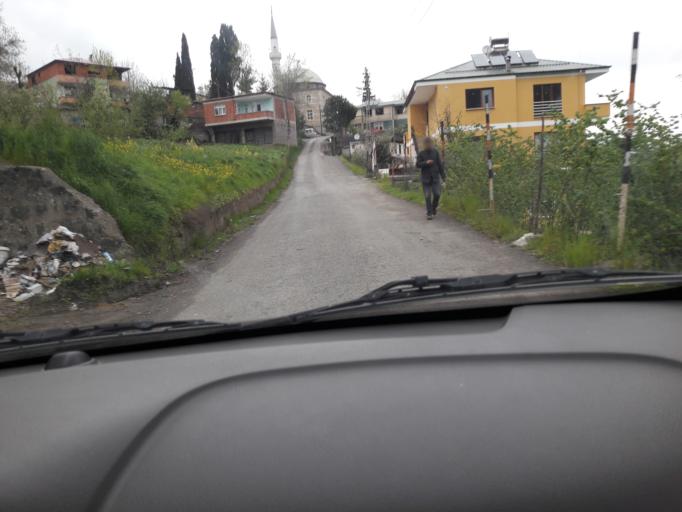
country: TR
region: Trabzon
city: Duzkoy
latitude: 40.9131
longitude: 39.4826
